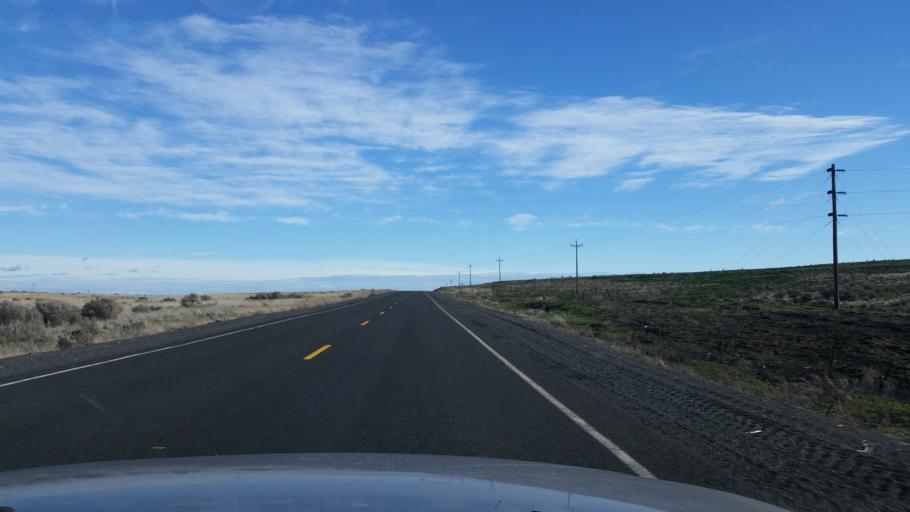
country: US
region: Washington
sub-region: Grant County
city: Warden
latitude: 47.3177
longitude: -118.8433
